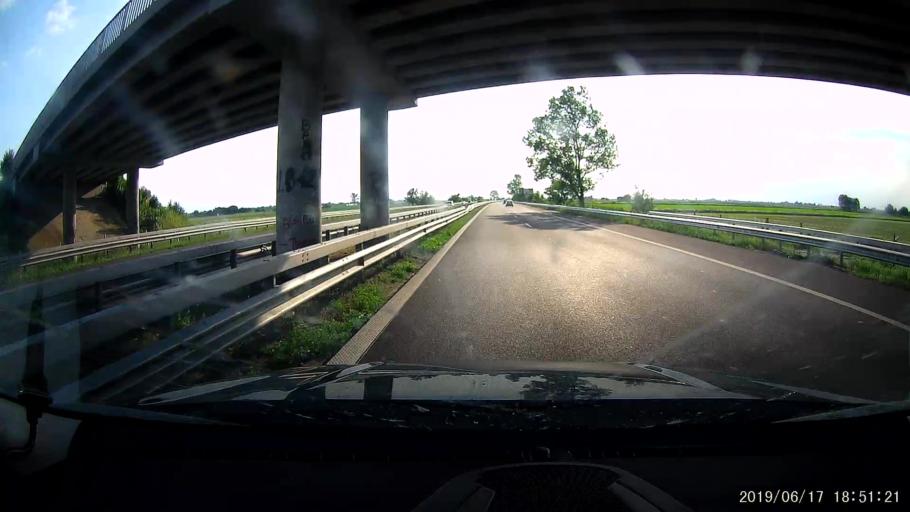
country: BG
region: Plovdiv
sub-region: Obshtina Rakovski
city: Rakovski
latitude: 42.2136
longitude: 24.9740
